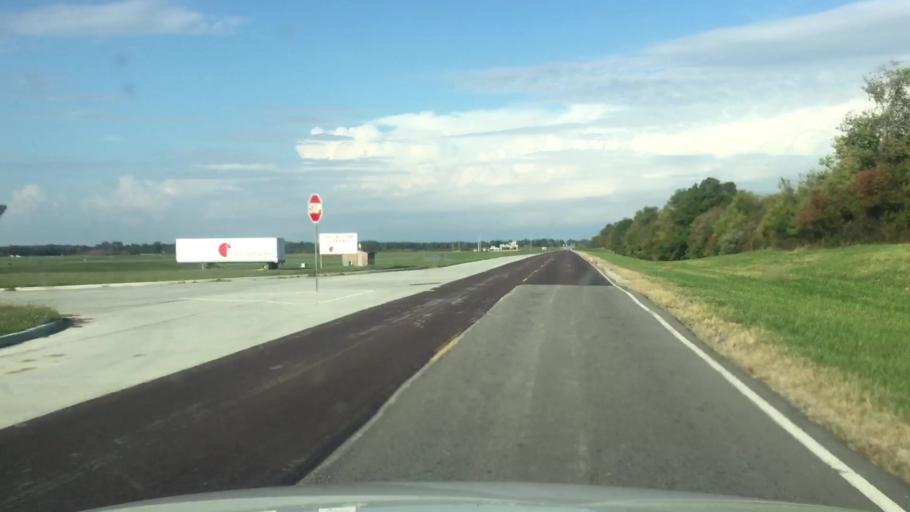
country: US
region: Missouri
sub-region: Boone County
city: Ashland
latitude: 38.8321
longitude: -92.2318
